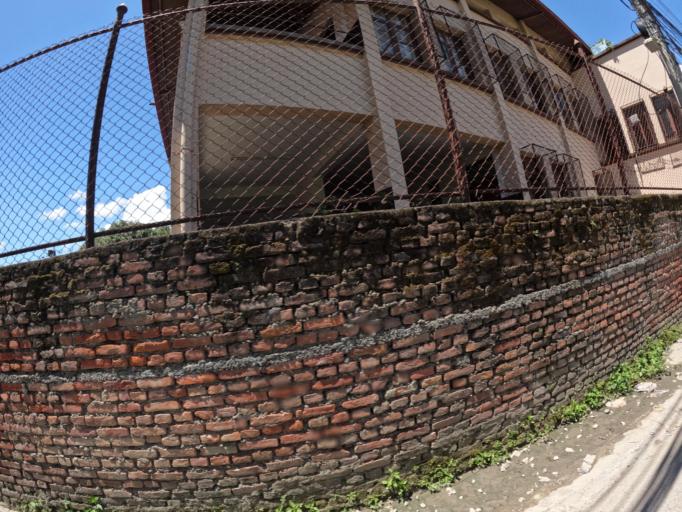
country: NP
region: Central Region
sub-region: Bagmati Zone
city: Kathmandu
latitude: 27.7470
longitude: 85.3264
